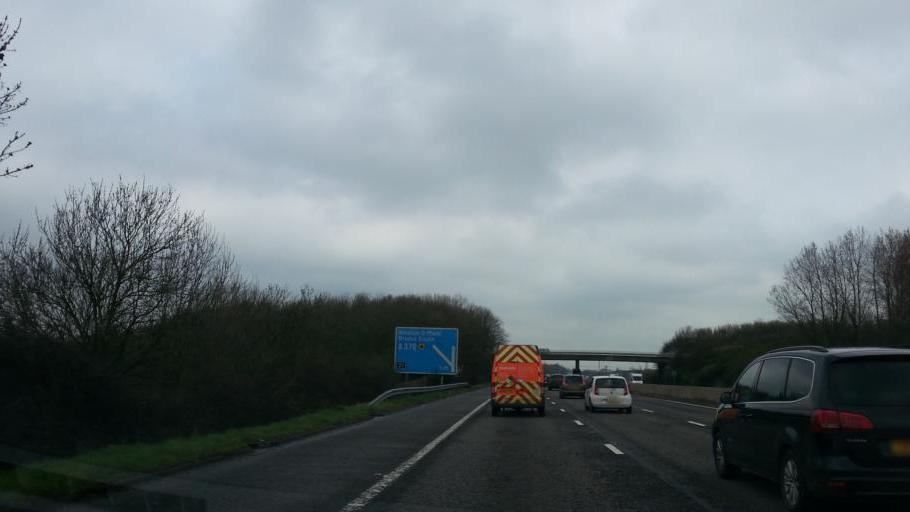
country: GB
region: England
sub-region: North Somerset
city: St. Georges
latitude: 51.3468
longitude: -2.8952
